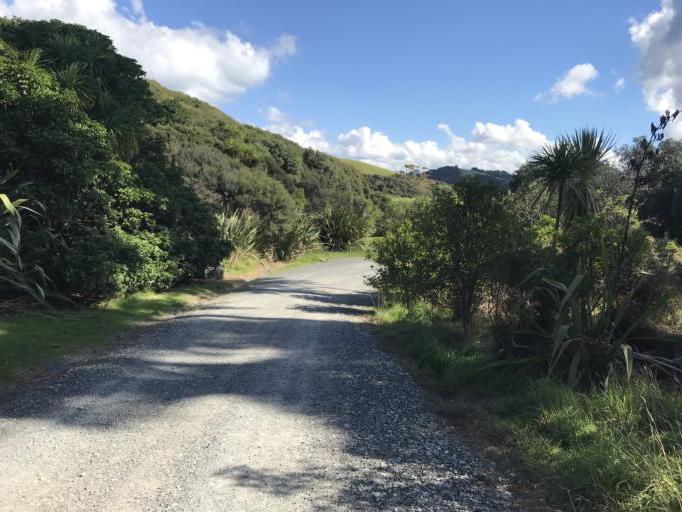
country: NZ
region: Auckland
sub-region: Auckland
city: Warkworth
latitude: -36.3696
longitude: 174.8341
